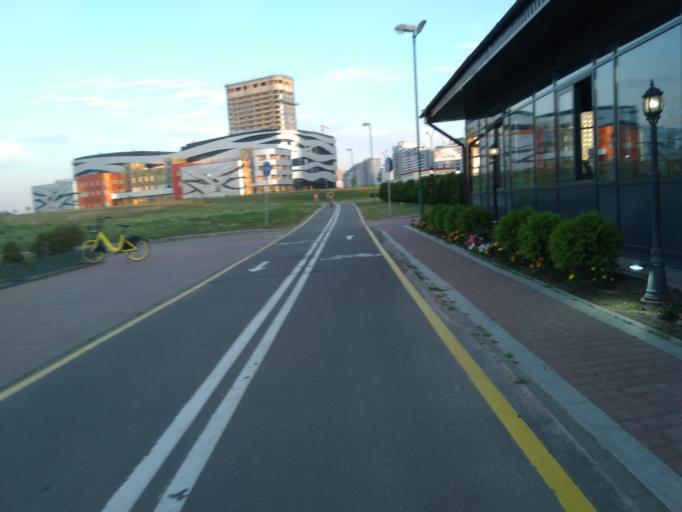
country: BY
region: Minsk
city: Zhdanovichy
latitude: 53.9433
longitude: 27.4656
